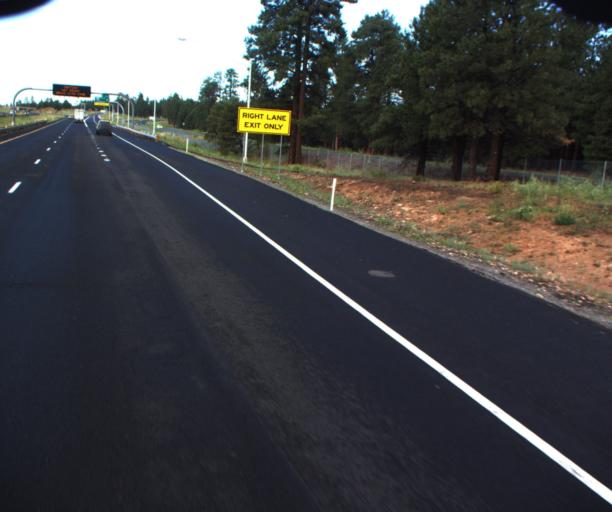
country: US
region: Arizona
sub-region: Coconino County
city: Kachina Village
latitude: 35.1474
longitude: -111.6828
